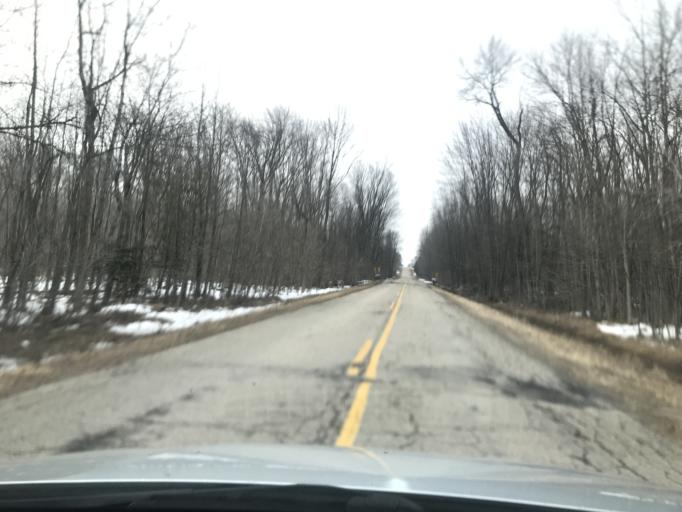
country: US
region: Wisconsin
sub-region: Oconto County
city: Oconto Falls
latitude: 44.8363
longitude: -88.1679
